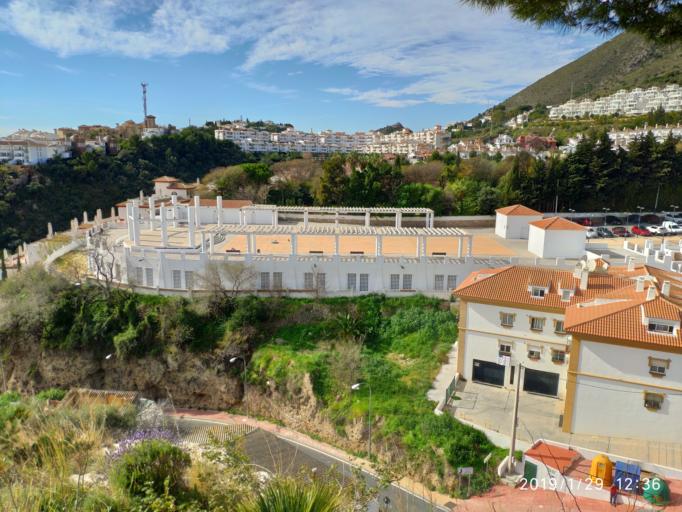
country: ES
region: Andalusia
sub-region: Provincia de Malaga
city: Benalmadena
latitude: 36.5926
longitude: -4.5729
